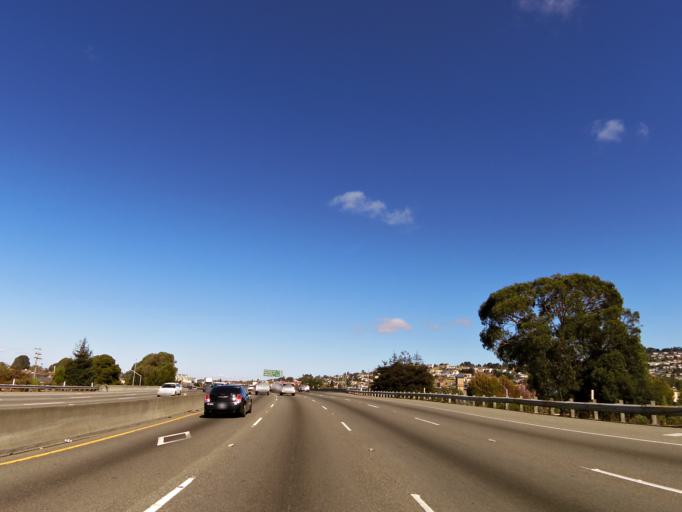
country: US
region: California
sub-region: Contra Costa County
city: El Cerrito
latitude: 37.9196
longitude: -122.3173
